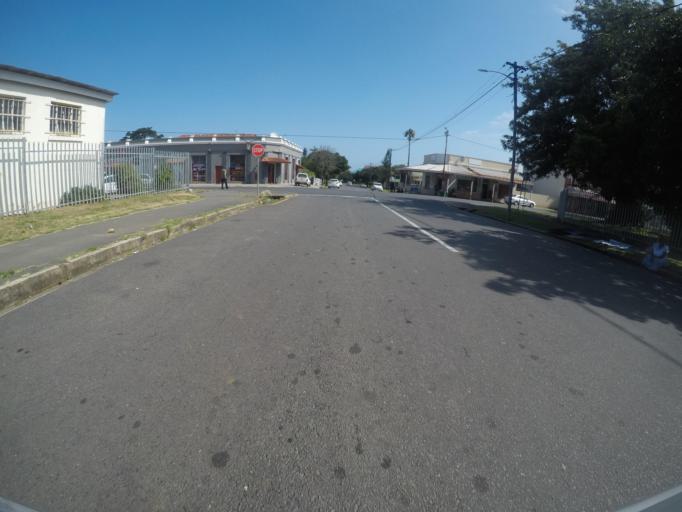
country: ZA
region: Eastern Cape
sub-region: Buffalo City Metropolitan Municipality
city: East London
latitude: -32.9749
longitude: 27.8868
